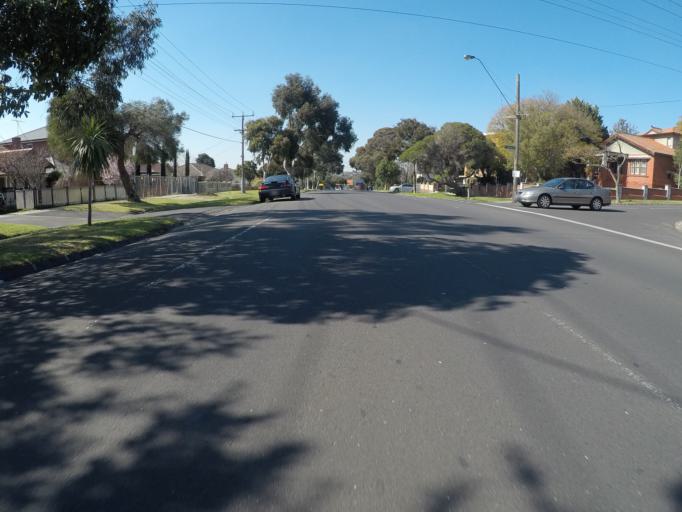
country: AU
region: Victoria
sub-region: Moreland
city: Pascoe Vale
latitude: -37.7473
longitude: 144.9233
